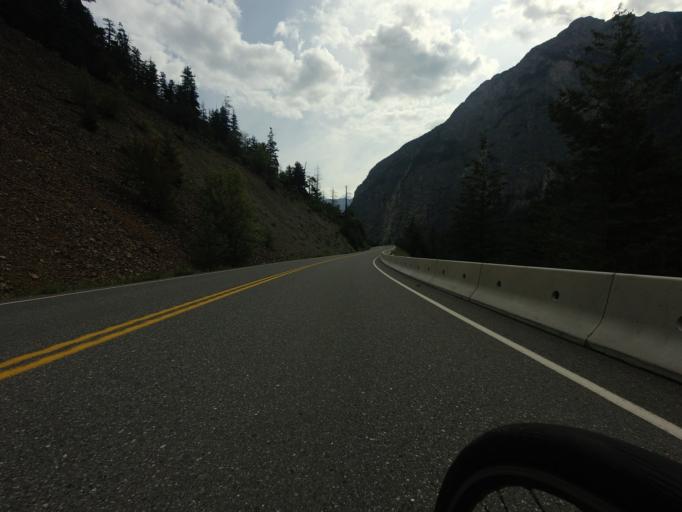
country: CA
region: British Columbia
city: Lillooet
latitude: 50.6581
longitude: -121.9953
